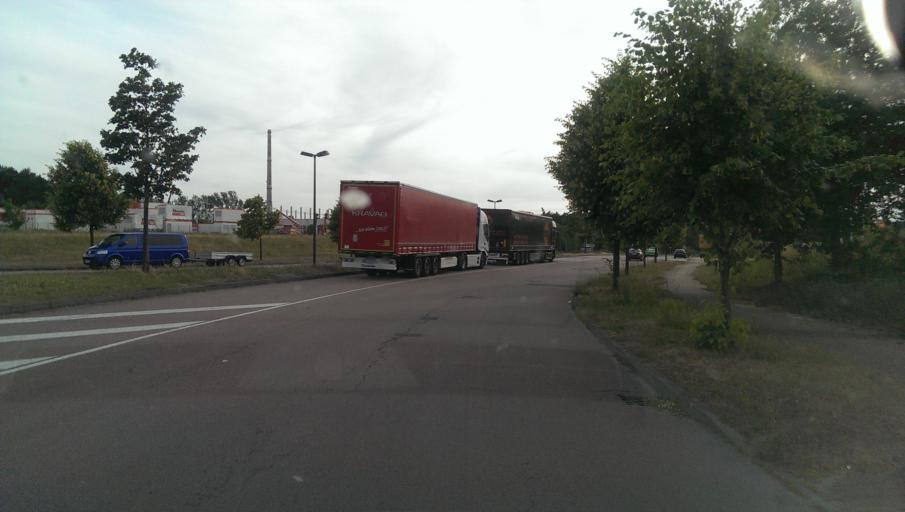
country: DE
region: Brandenburg
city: Ludwigsfelde
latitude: 52.3197
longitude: 13.2925
